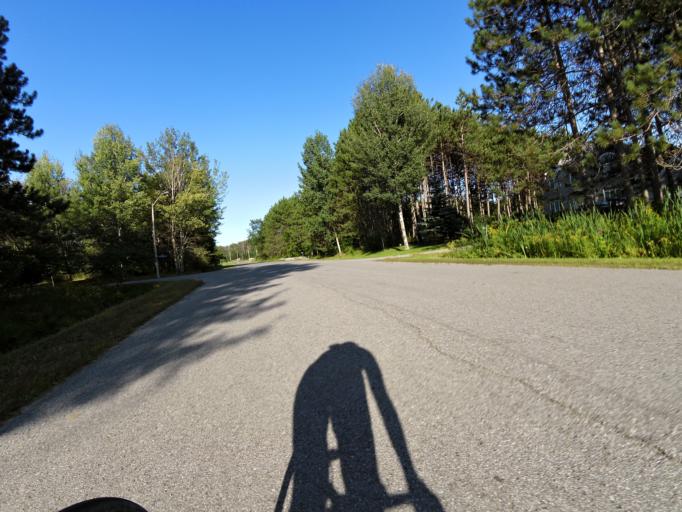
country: CA
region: Ontario
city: Bells Corners
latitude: 45.4676
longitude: -76.0322
